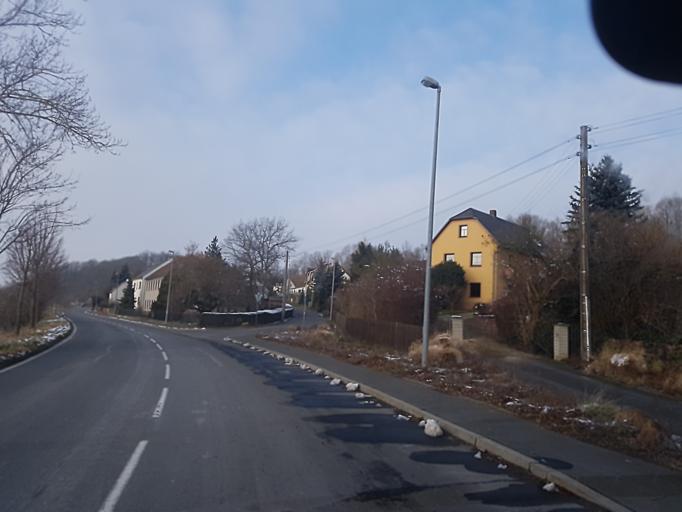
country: DE
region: Saxony
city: Leisnig
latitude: 51.1681
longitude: 12.9230
